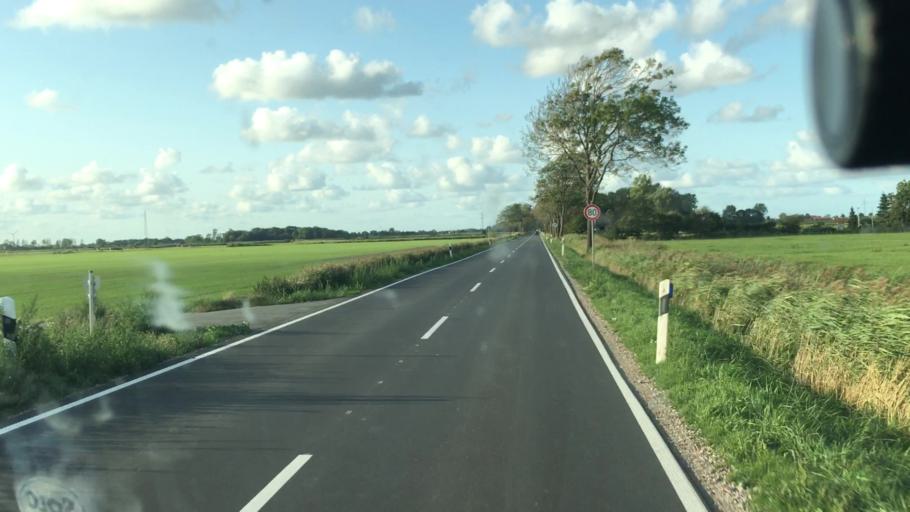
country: DE
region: Lower Saxony
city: Jever
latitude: 53.6276
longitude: 7.8617
